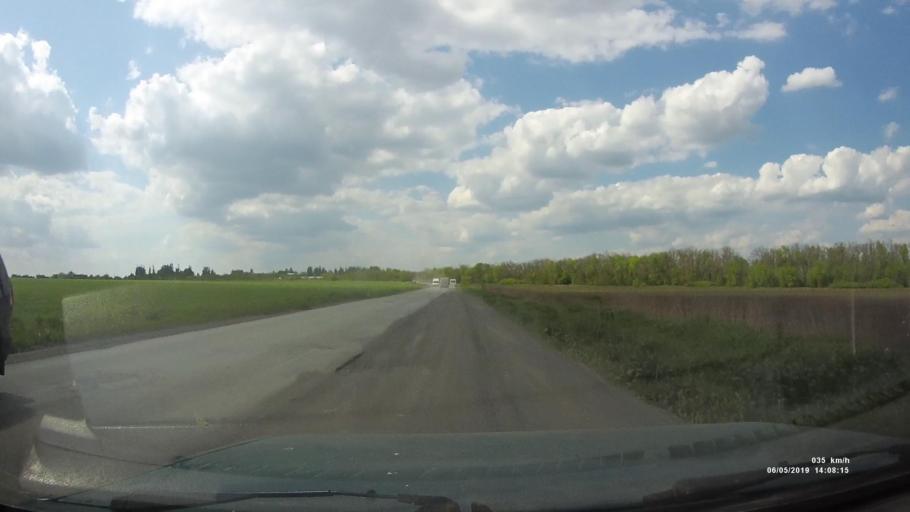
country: RU
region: Rostov
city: Shakhty
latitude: 47.6826
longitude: 40.2994
